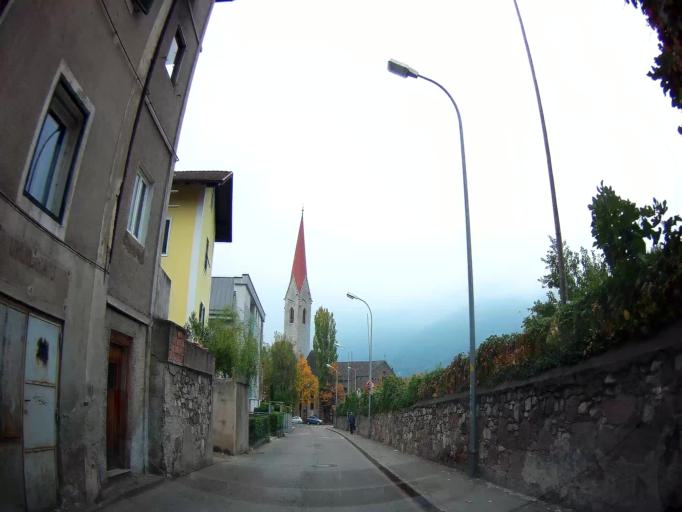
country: IT
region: Trentino-Alto Adige
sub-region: Bolzano
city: Merano
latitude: 46.6626
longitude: 11.1628
